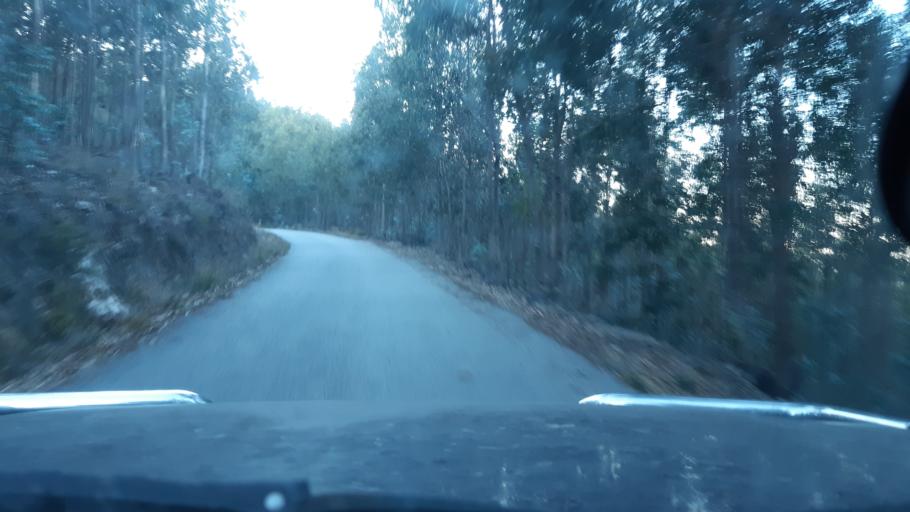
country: PT
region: Aveiro
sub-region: Agueda
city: Aguada de Cima
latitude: 40.5485
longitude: -8.2809
